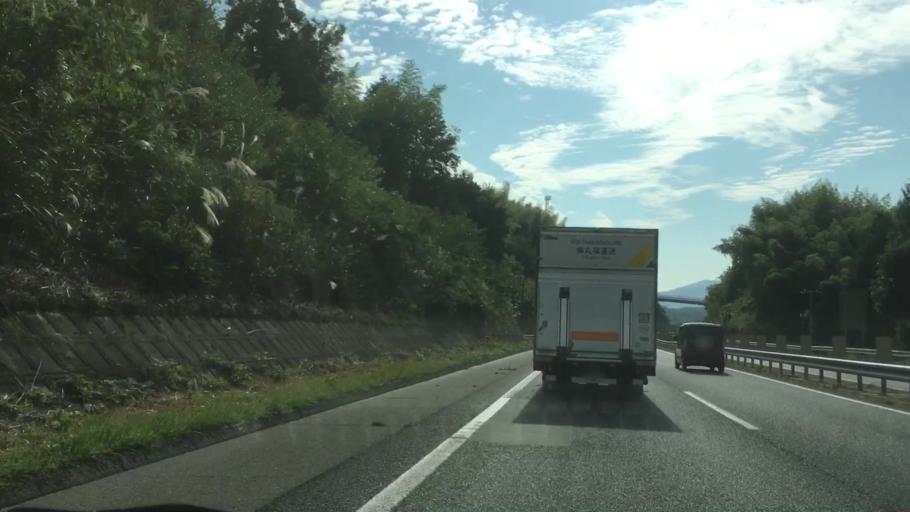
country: JP
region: Yamaguchi
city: Yanai
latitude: 34.0861
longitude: 132.0898
